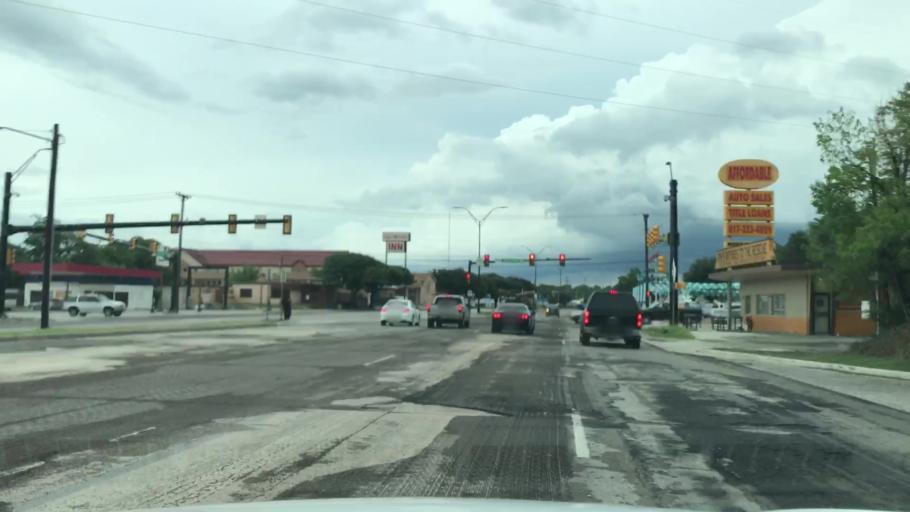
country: US
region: Texas
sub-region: Tarrant County
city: Fort Worth
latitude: 32.7461
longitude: -97.3040
